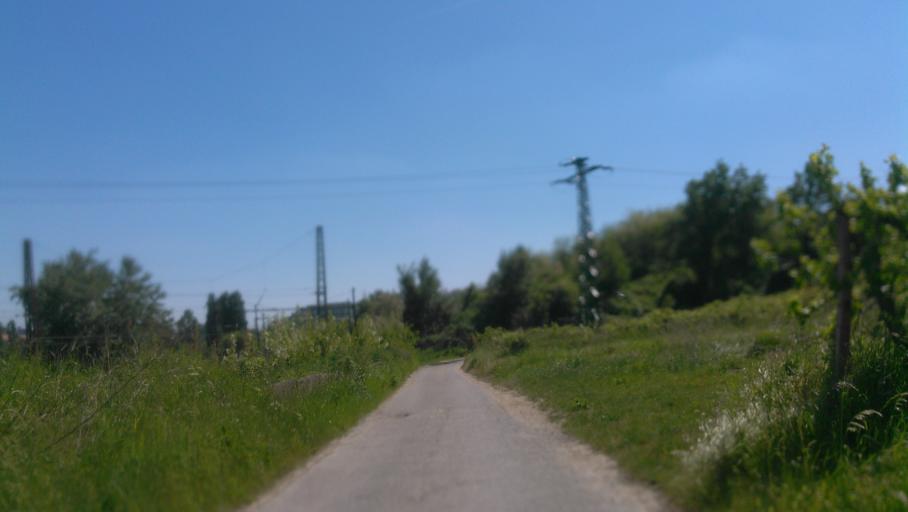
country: SK
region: Bratislavsky
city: Bratislava
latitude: 48.1811
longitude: 17.1240
